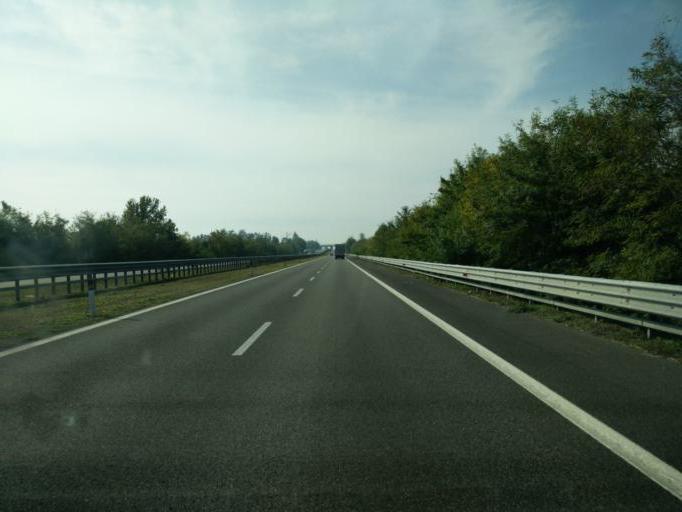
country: IT
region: Lombardy
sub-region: Provincia di Cremona
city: Corte de' Frati
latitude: 45.2451
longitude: 10.1204
